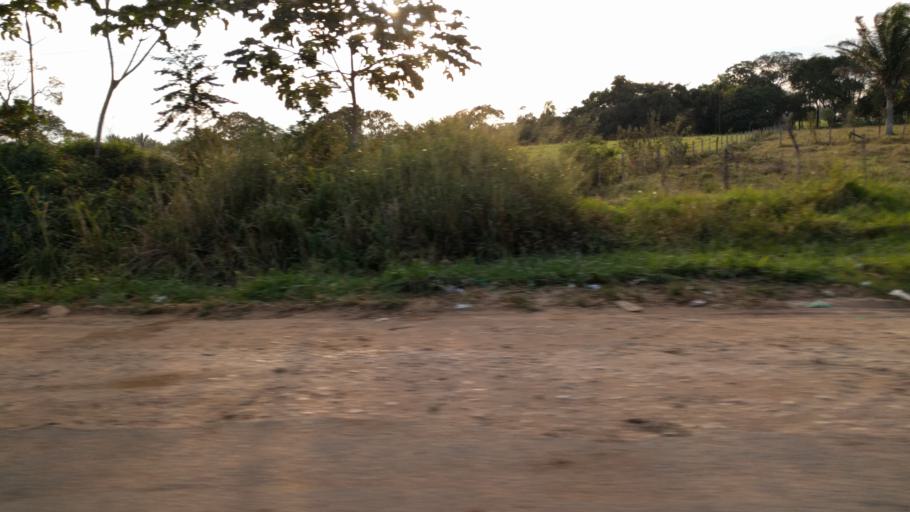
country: BO
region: Santa Cruz
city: Buena Vista
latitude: -17.4242
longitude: -63.6263
